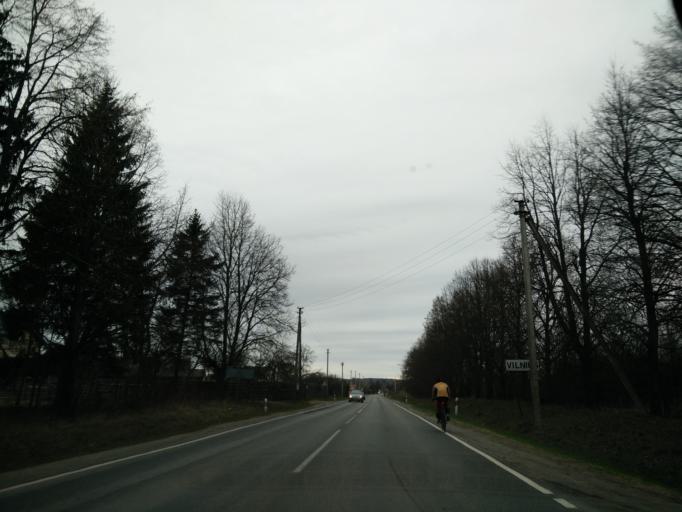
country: LT
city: Skaidiskes
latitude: 54.6918
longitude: 25.4643
